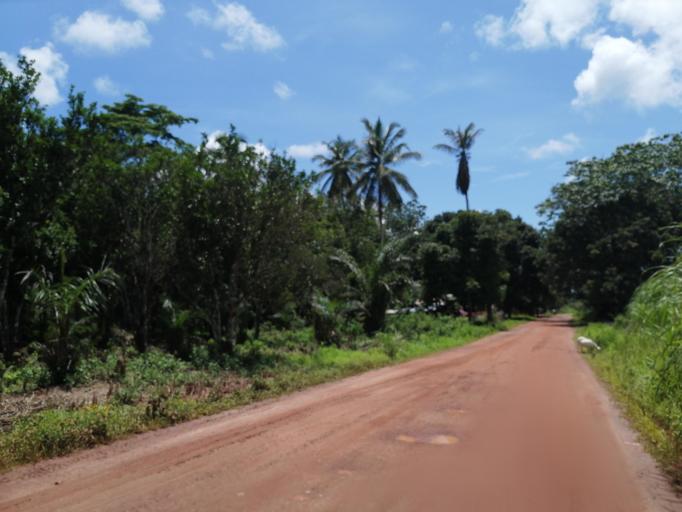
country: SL
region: Northern Province
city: Pepel
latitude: 8.6807
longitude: -12.9997
